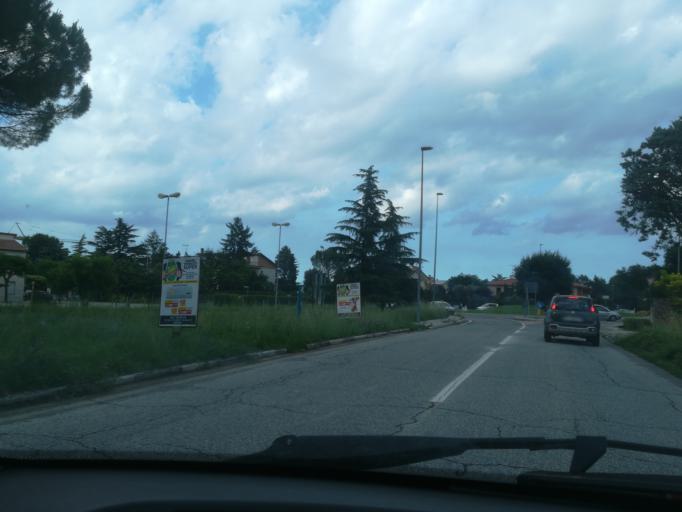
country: IT
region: The Marches
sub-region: Provincia di Macerata
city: Zona Industriale
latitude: 43.2598
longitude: 13.4952
